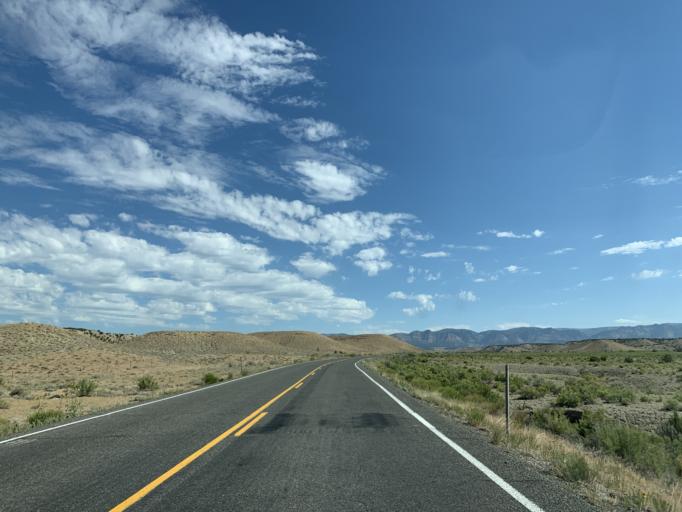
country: US
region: Utah
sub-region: Carbon County
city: Wellington
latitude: 39.5635
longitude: -110.6566
